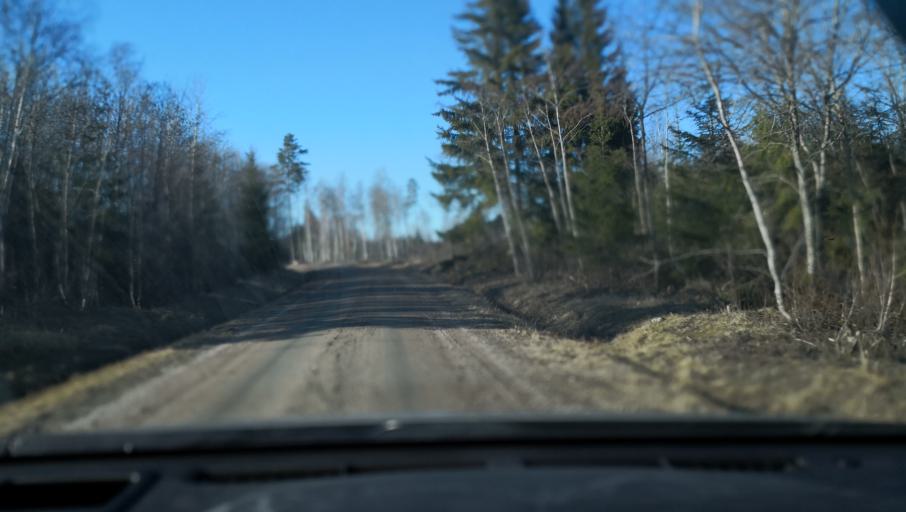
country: SE
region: Dalarna
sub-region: Avesta Kommun
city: Horndal
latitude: 60.1760
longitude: 16.6315
